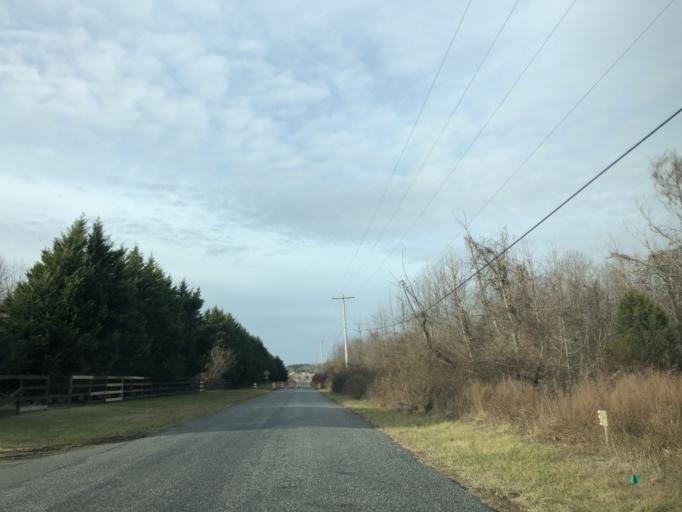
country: US
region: Delaware
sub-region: New Castle County
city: Middletown
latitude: 39.4532
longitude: -75.6413
